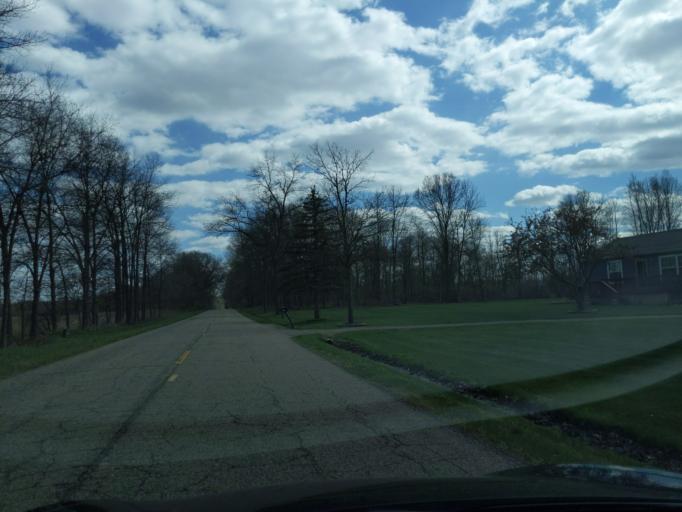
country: US
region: Michigan
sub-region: Ingham County
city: Leslie
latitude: 42.4156
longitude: -84.5268
